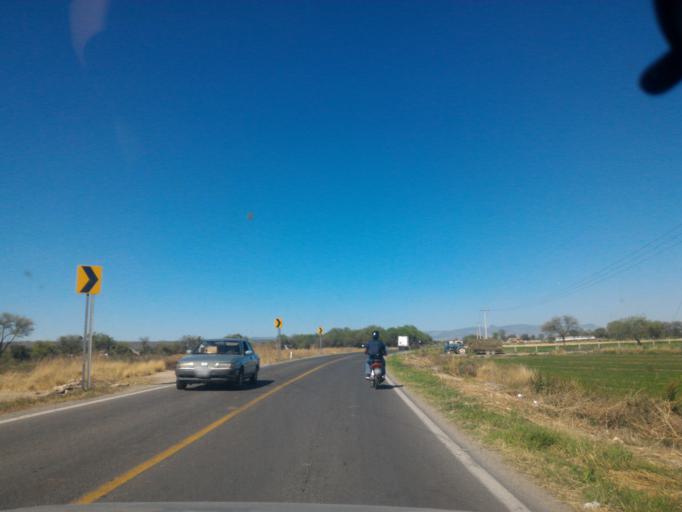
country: MX
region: Guanajuato
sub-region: San Francisco del Rincon
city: San Roque de Montes
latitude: 21.0109
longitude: -101.8014
